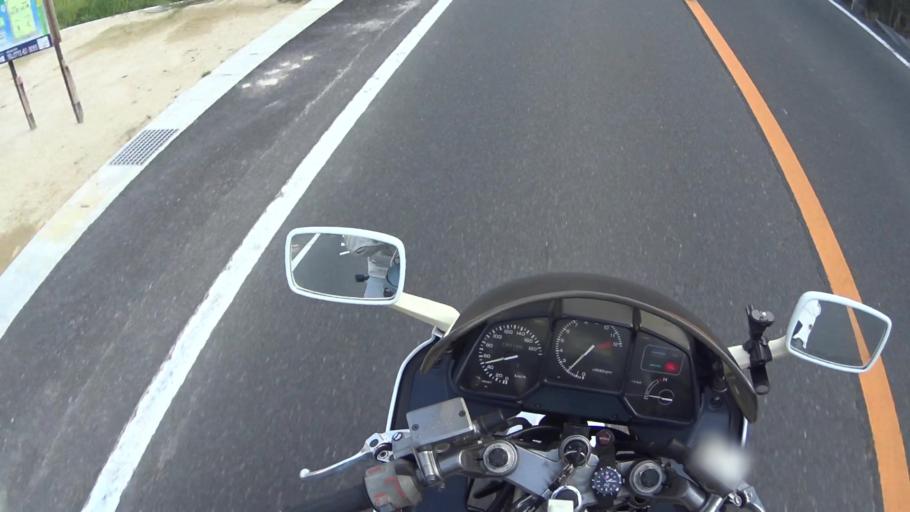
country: JP
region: Kyoto
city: Miyazu
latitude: 35.6068
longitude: 135.0877
